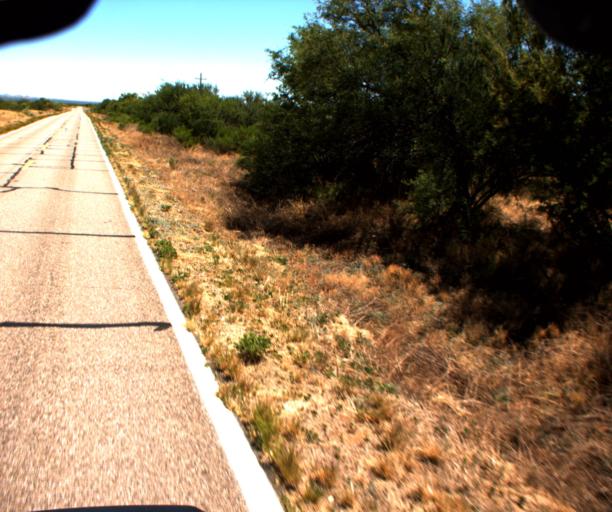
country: US
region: Arizona
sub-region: Pima County
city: Three Points
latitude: 31.7025
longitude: -111.4875
